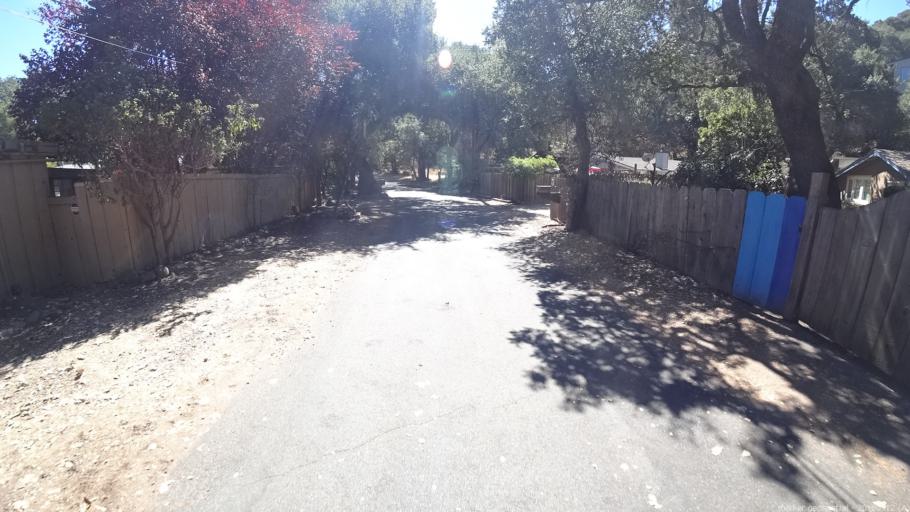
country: US
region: California
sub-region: Monterey County
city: Carmel Valley Village
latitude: 36.4723
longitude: -121.7264
